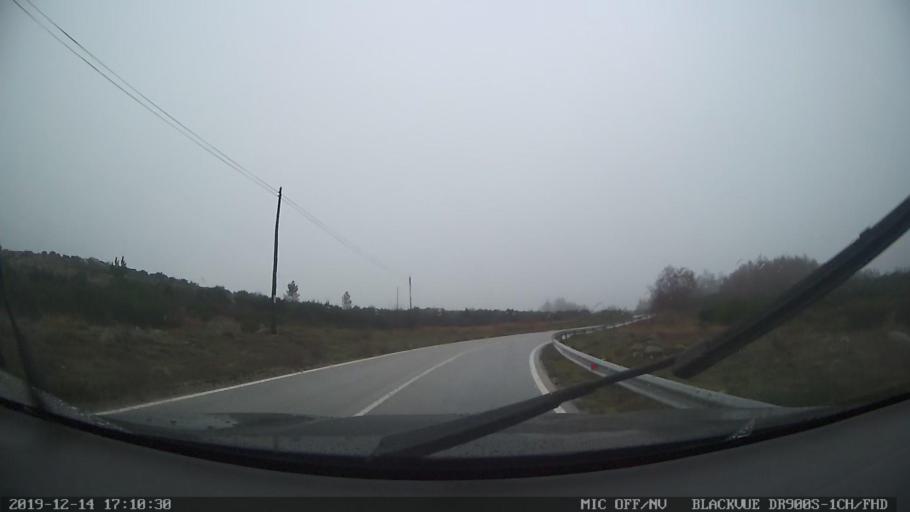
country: PT
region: Vila Real
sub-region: Vila Pouca de Aguiar
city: Vila Pouca de Aguiar
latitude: 41.4810
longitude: -7.6100
